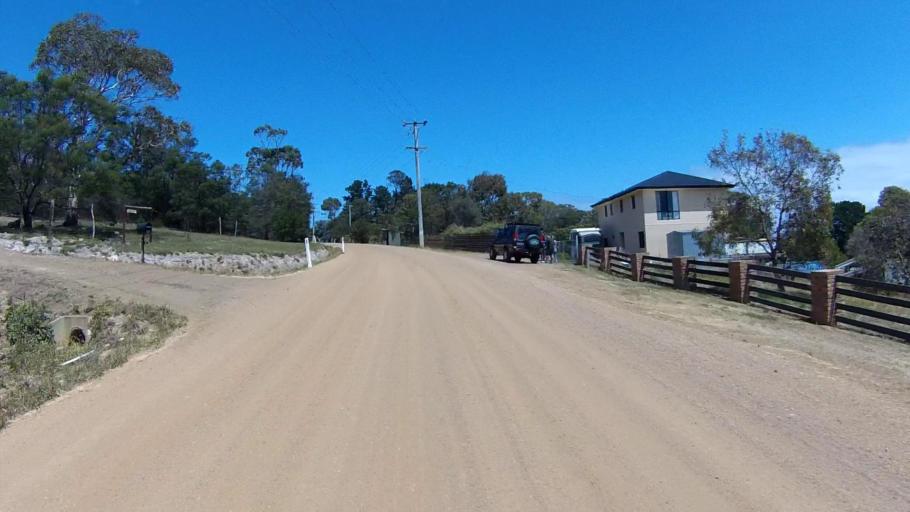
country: AU
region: Tasmania
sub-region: Clarence
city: Lauderdale
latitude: -42.9371
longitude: 147.4607
